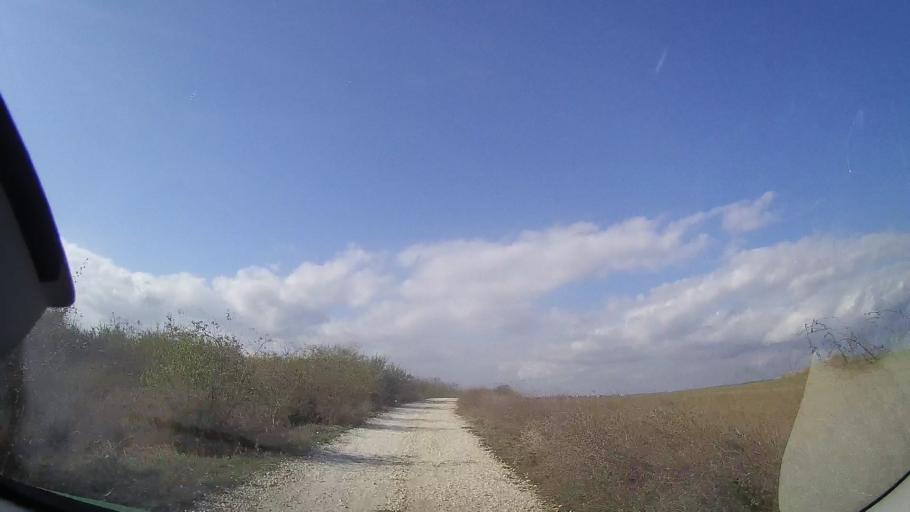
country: RO
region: Constanta
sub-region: Comuna Douazeci si Trei August
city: Douazeci si Trei August
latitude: 43.9047
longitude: 28.6175
